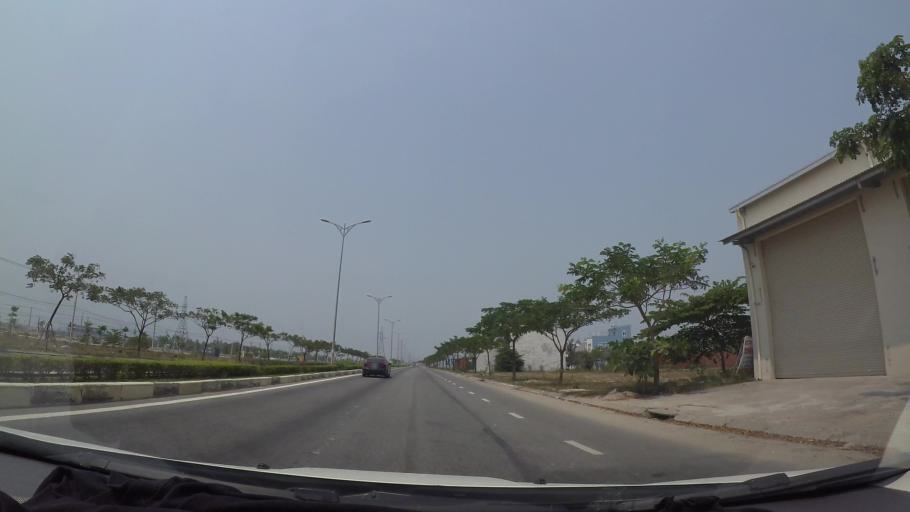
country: VN
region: Da Nang
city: Ngu Hanh Son
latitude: 15.9946
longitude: 108.2357
